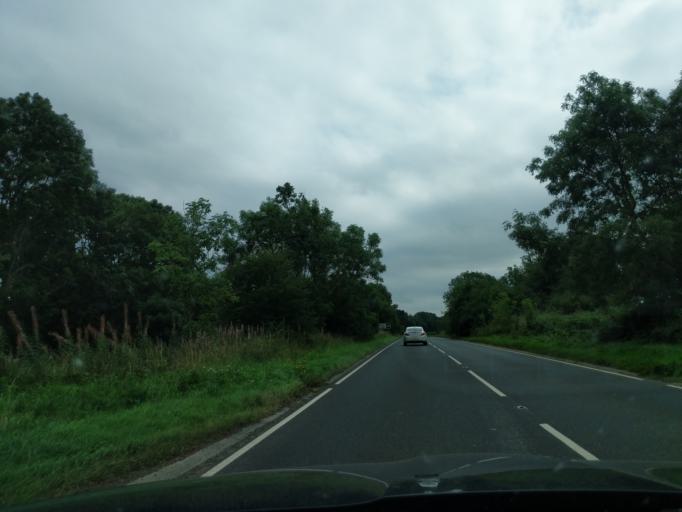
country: GB
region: England
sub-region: Northumberland
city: Wooler
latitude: 55.4914
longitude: -1.9444
